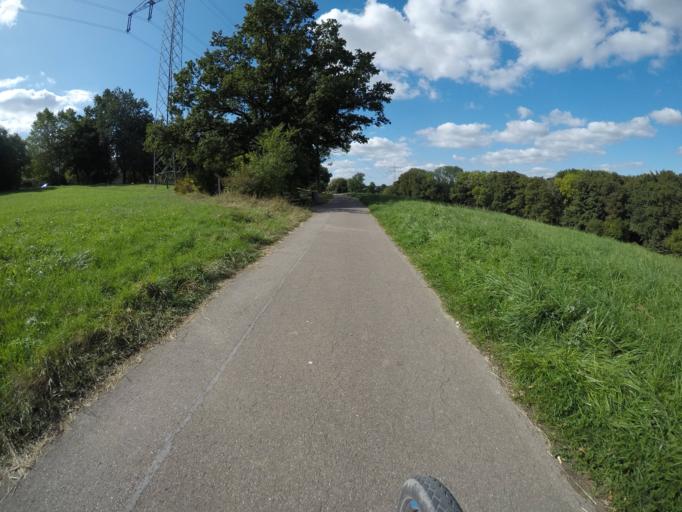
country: DE
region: Baden-Wuerttemberg
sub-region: Regierungsbezirk Stuttgart
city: Leinfelden-Echterdingen
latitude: 48.7161
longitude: 9.1553
